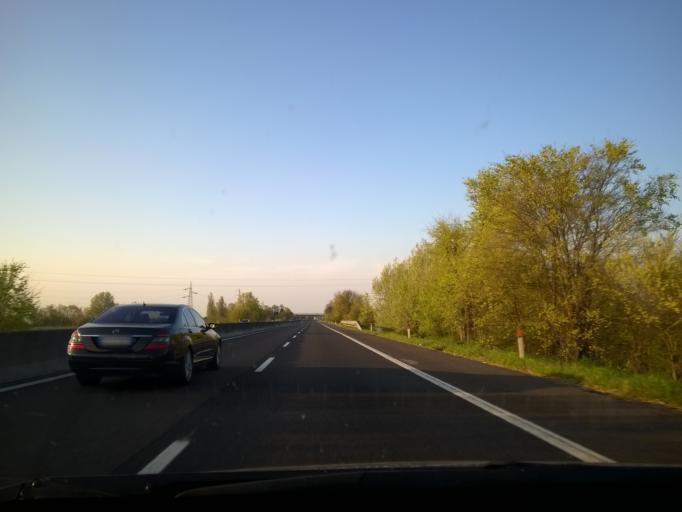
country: IT
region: Emilia-Romagna
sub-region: Provincia di Ferrara
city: Porotto-Cassama
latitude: 44.8099
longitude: 11.5544
